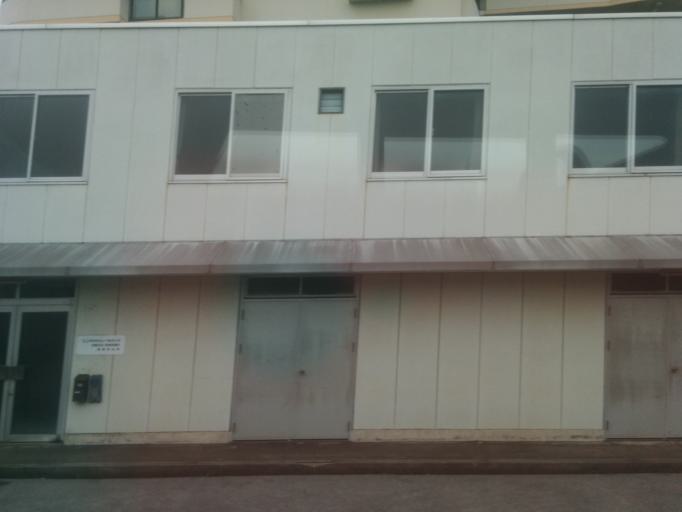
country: JP
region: Shiga Prefecture
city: Hikone
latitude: 35.2745
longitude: 136.2638
